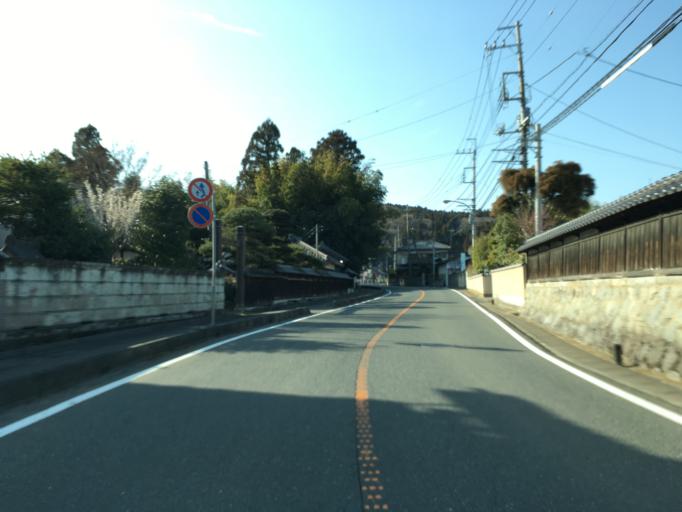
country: JP
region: Ibaraki
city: Takahagi
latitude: 36.7227
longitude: 140.6747
